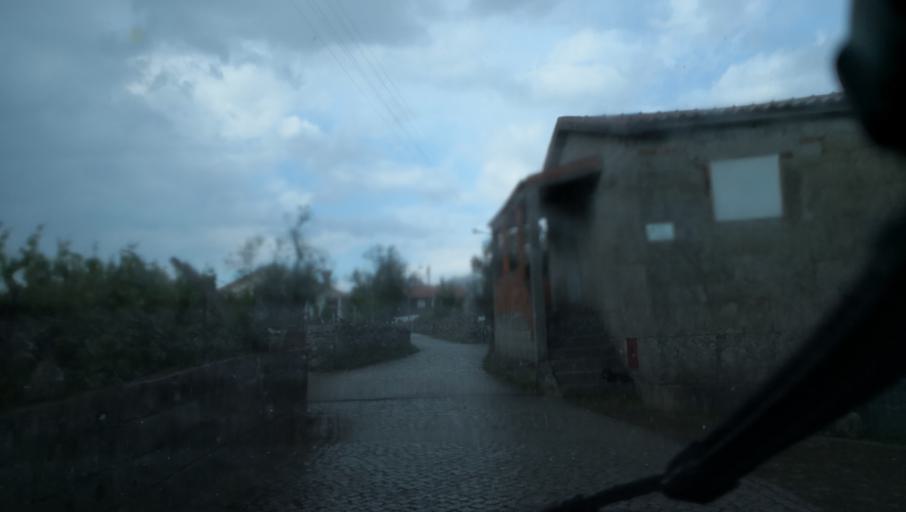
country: PT
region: Vila Real
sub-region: Vila Real
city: Vila Real
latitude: 41.3580
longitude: -7.6987
